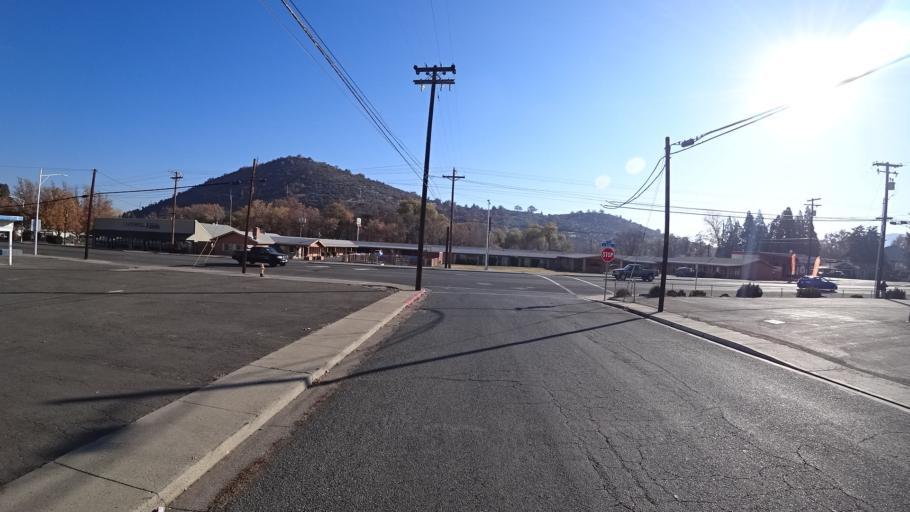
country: US
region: California
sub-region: Siskiyou County
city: Yreka
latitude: 41.7207
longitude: -122.6398
